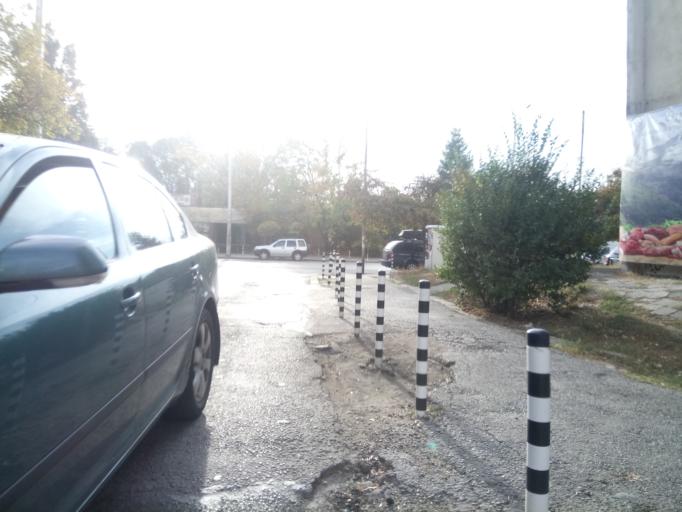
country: BG
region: Sofia-Capital
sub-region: Stolichna Obshtina
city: Sofia
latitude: 42.6828
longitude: 23.3556
